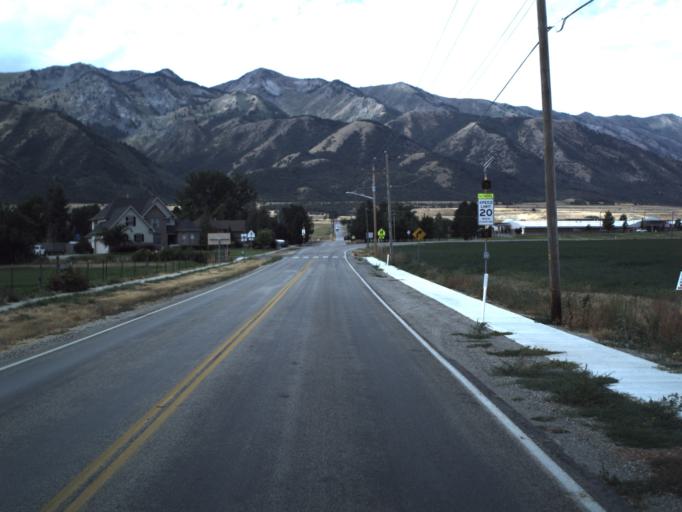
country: US
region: Utah
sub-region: Cache County
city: Wellsville
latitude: 41.6487
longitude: -111.9353
